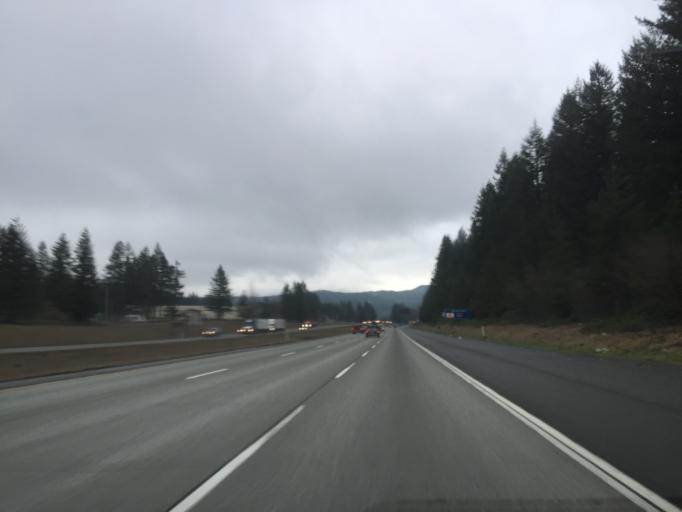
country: US
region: Washington
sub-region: King County
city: Tanner
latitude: 47.4721
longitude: -121.7375
